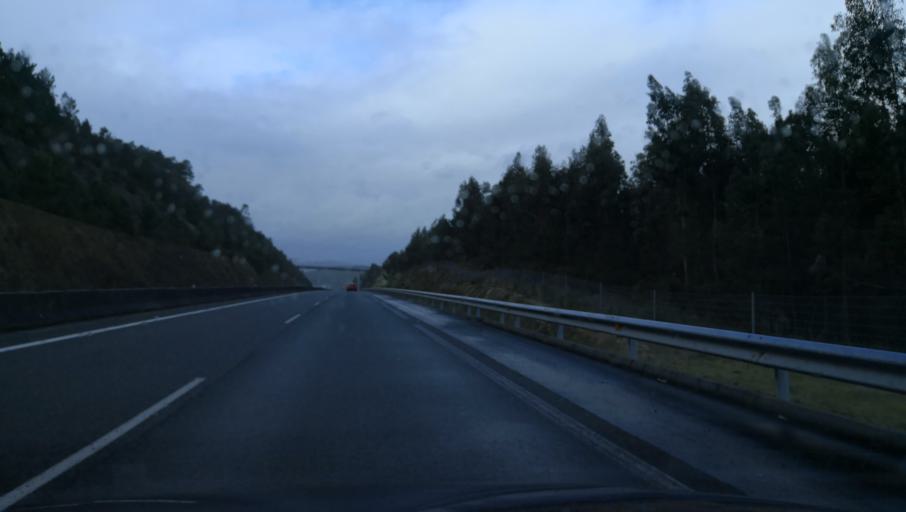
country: ES
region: Galicia
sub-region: Provincia da Coruna
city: Ribeira
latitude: 42.7356
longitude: -8.3662
